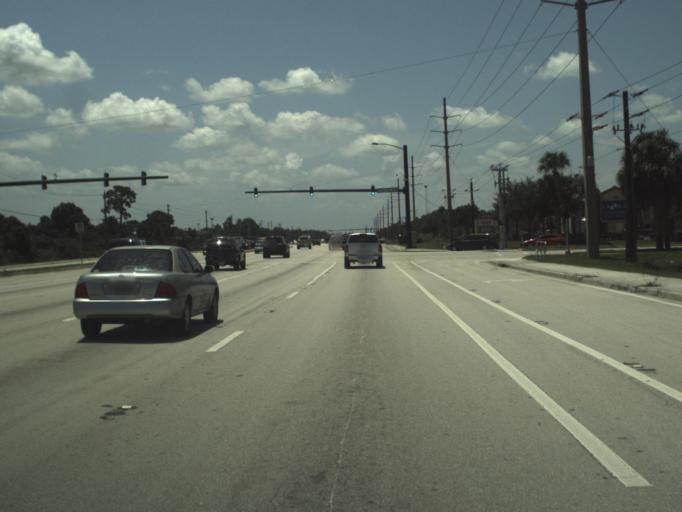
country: US
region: Florida
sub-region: Martin County
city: North River Shores
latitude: 27.2598
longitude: -80.2820
